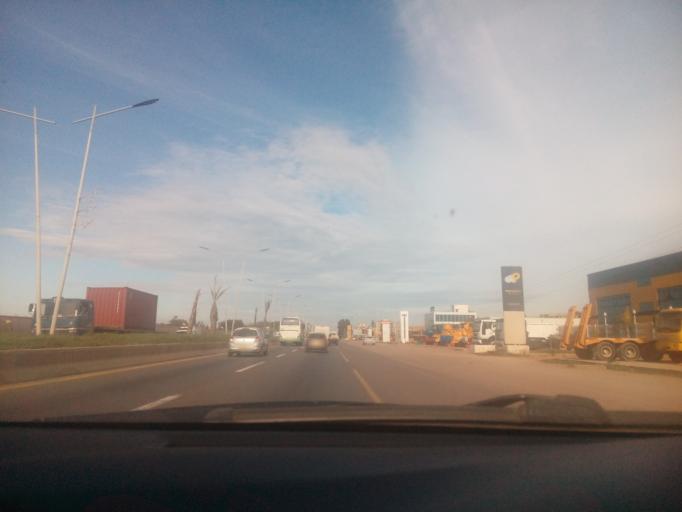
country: DZ
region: Oran
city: Es Senia
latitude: 35.6197
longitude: -0.5845
